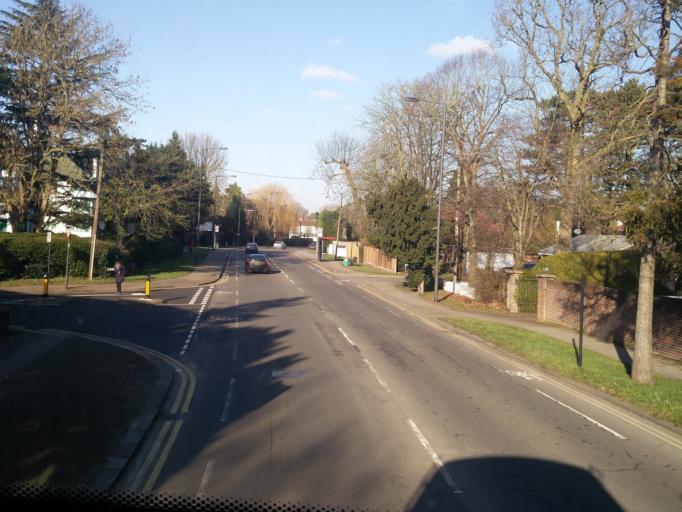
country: GB
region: England
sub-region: Greater London
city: Pinner
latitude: 51.5978
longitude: -0.3901
